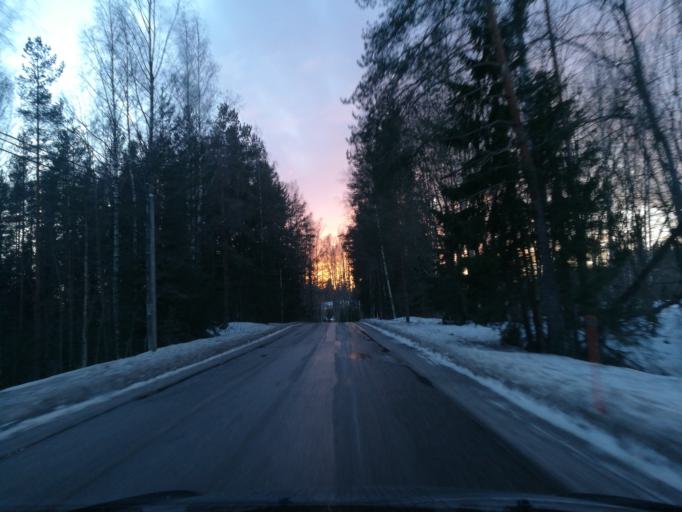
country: FI
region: Uusimaa
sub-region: Helsinki
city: Kerava
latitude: 60.3972
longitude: 25.1647
